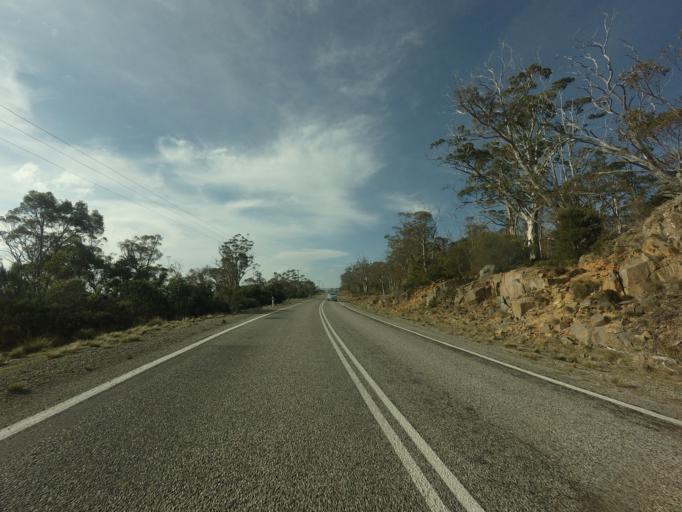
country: AU
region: Tasmania
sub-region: Meander Valley
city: Deloraine
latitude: -41.9864
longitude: 146.7114
